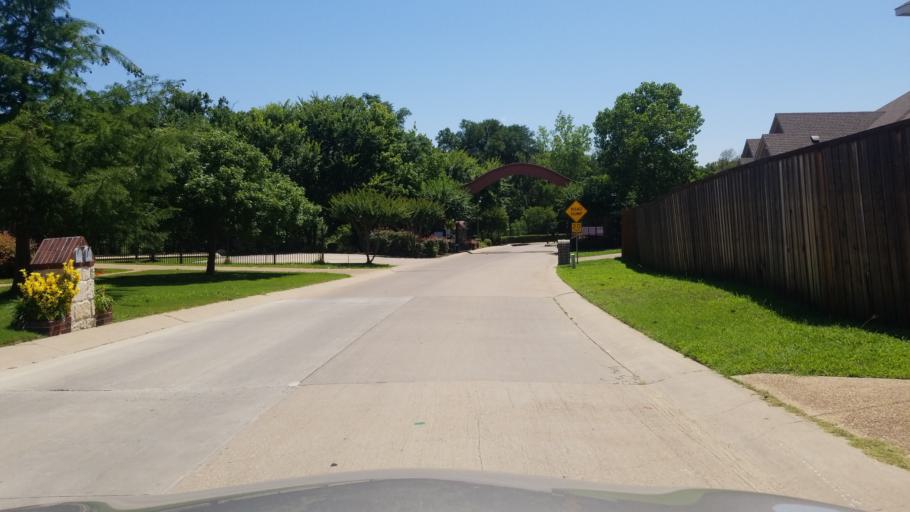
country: US
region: Texas
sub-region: Dallas County
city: Grand Prairie
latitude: 32.6793
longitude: -96.9994
